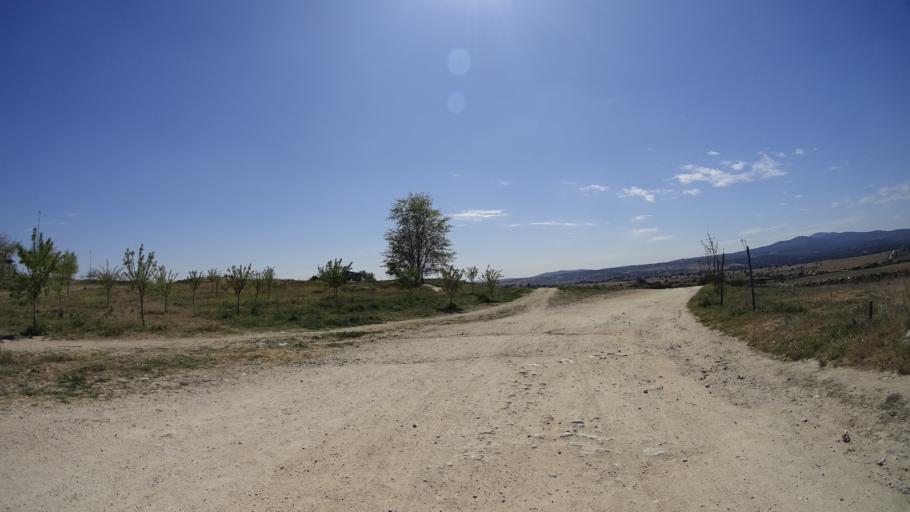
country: ES
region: Madrid
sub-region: Provincia de Madrid
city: Colmenar Viejo
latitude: 40.6649
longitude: -3.7865
